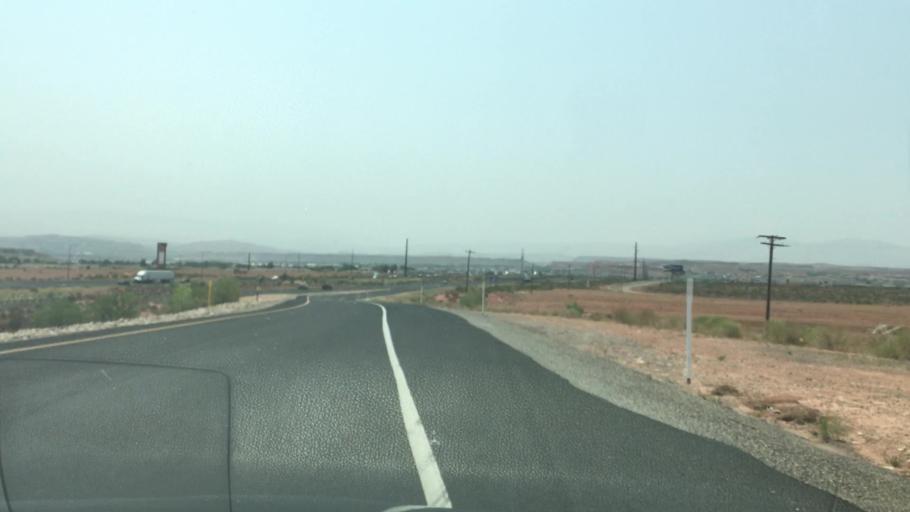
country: US
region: Utah
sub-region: Washington County
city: Washington
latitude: 37.1480
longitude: -113.4890
